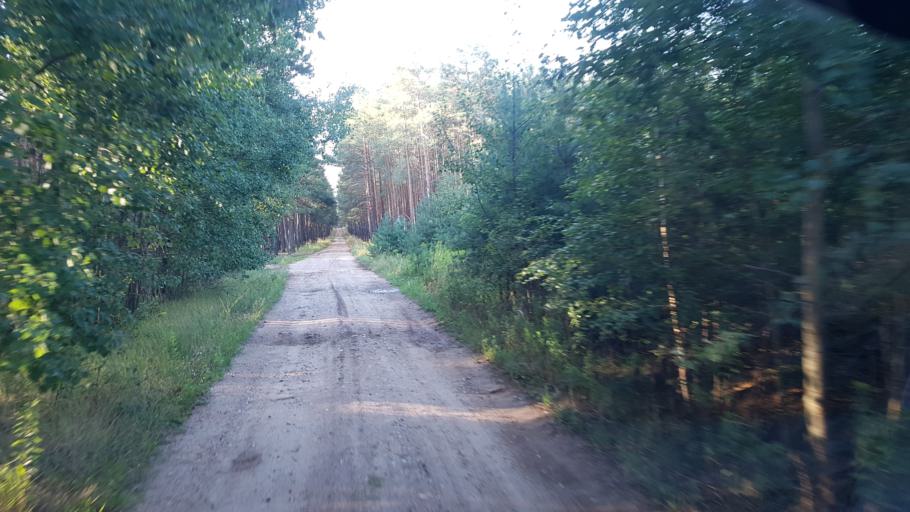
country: DE
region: Brandenburg
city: Sonnewalde
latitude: 51.6474
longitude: 13.6482
